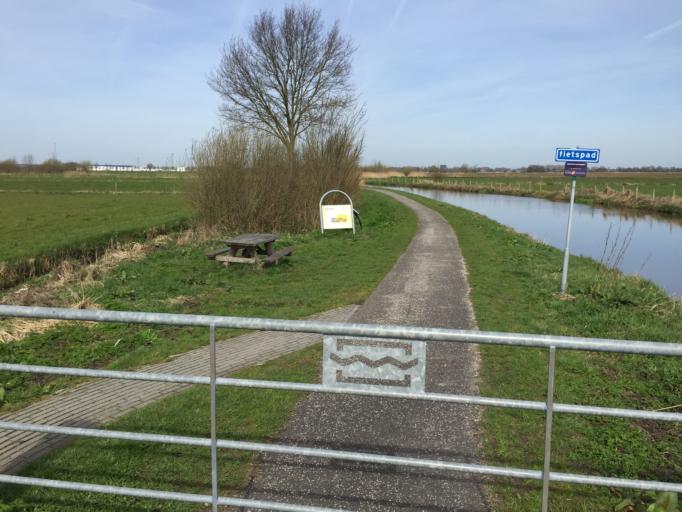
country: NL
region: Utrecht
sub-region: Gemeente Rhenen
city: Rhenen
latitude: 51.9957
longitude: 5.6013
